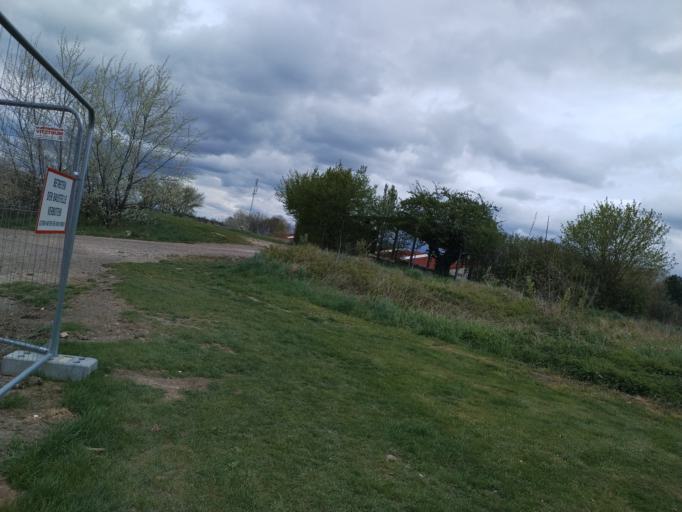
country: AT
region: Lower Austria
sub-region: Politischer Bezirk Korneuburg
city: Stockerau
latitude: 48.3961
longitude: 16.2160
